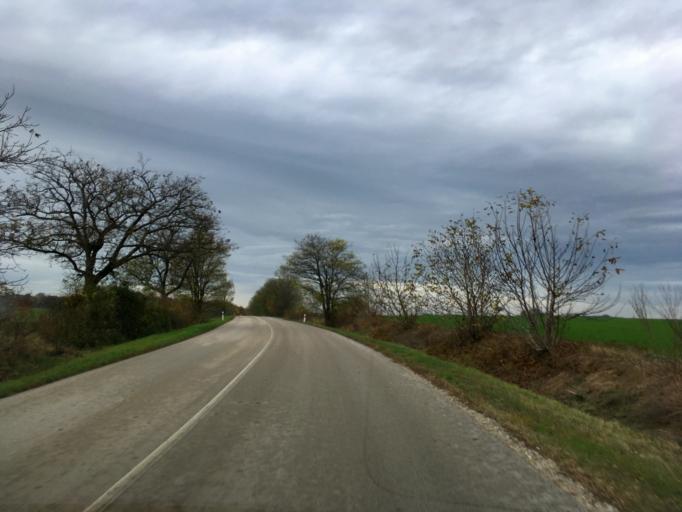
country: SK
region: Nitriansky
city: Svodin
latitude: 48.0289
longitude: 18.3981
